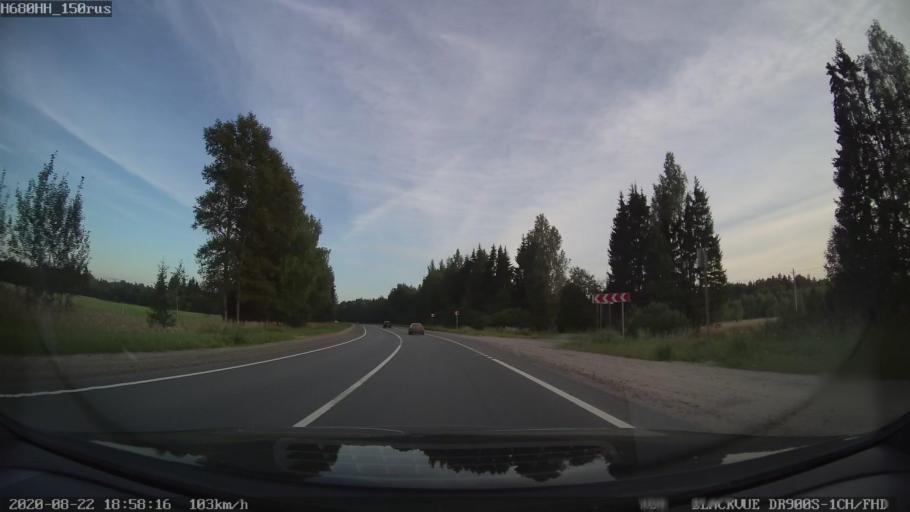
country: RU
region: Tverskaya
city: Rameshki
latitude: 57.1557
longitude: 36.0754
